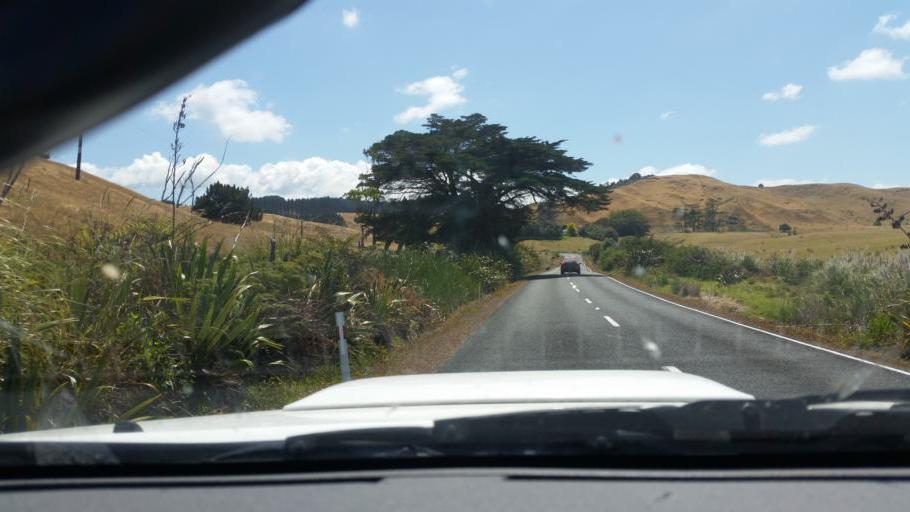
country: NZ
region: Northland
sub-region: Kaipara District
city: Dargaville
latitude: -35.8261
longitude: 173.6753
